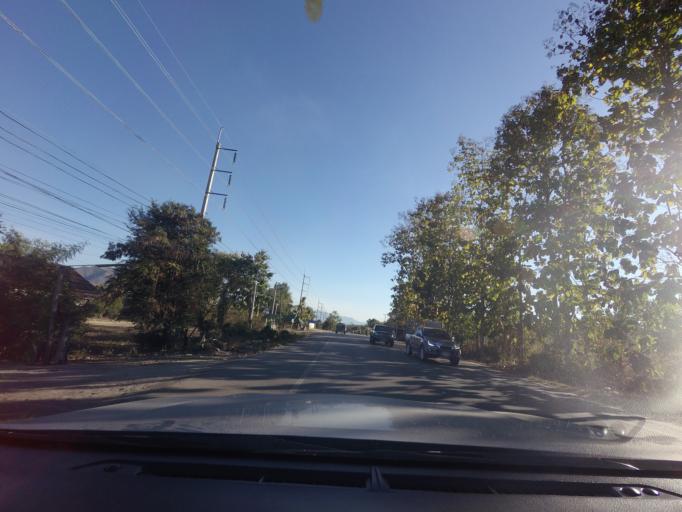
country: TH
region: Mae Hong Son
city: Wiang Nuea
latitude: 19.3833
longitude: 98.4267
